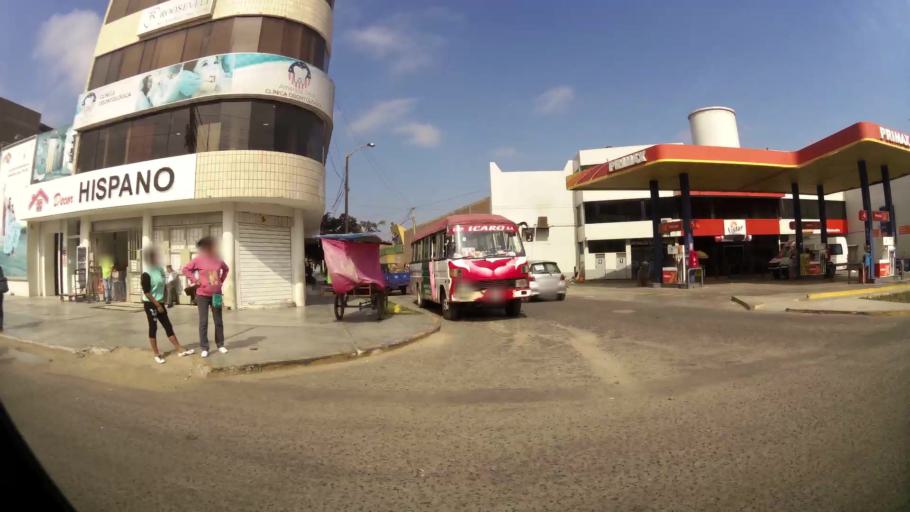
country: PE
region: La Libertad
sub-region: Provincia de Trujillo
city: Trujillo
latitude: -8.1143
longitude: -79.0147
